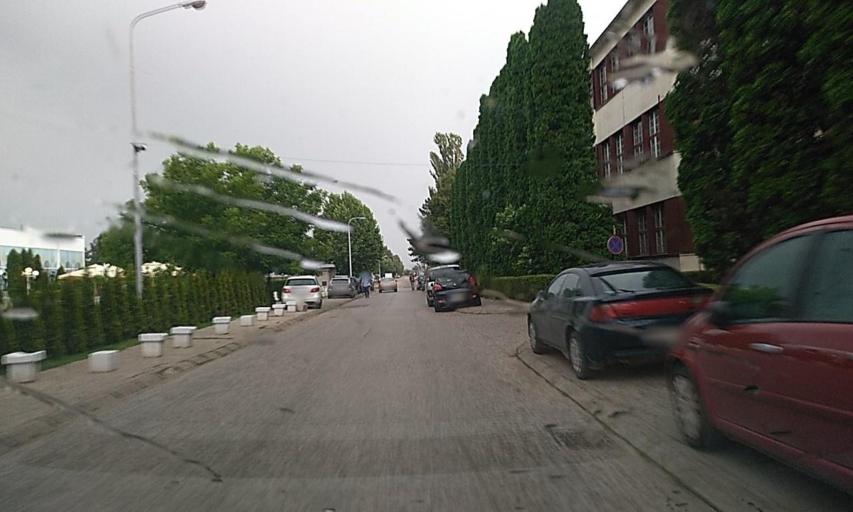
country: RS
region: Central Serbia
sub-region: Nisavski Okrug
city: Nis
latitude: 43.3058
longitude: 21.9489
